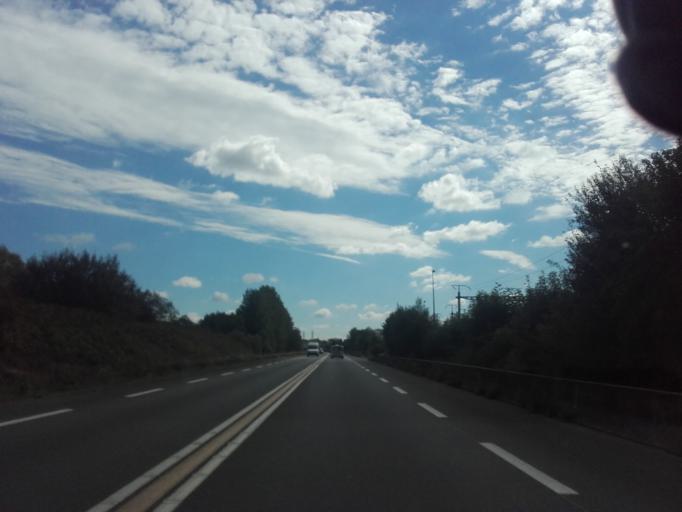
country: FR
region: Bourgogne
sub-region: Departement de Saone-et-Loire
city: Charnay-les-Macon
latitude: 46.2965
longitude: 4.7699
